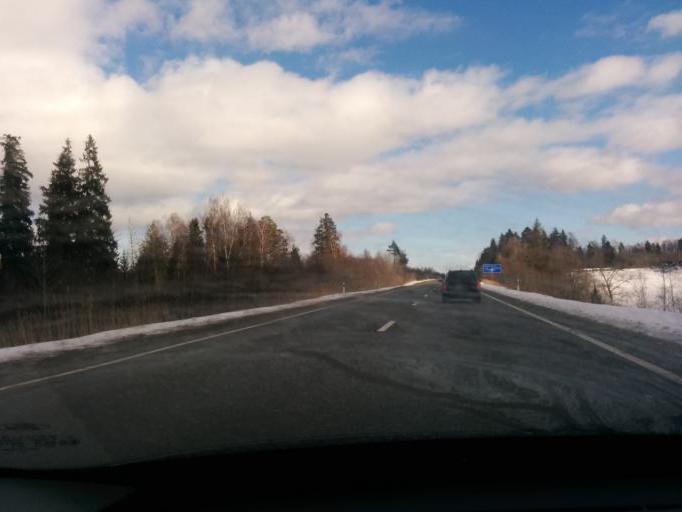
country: LV
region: Raunas
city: Rauna
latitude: 57.3060
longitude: 25.6186
